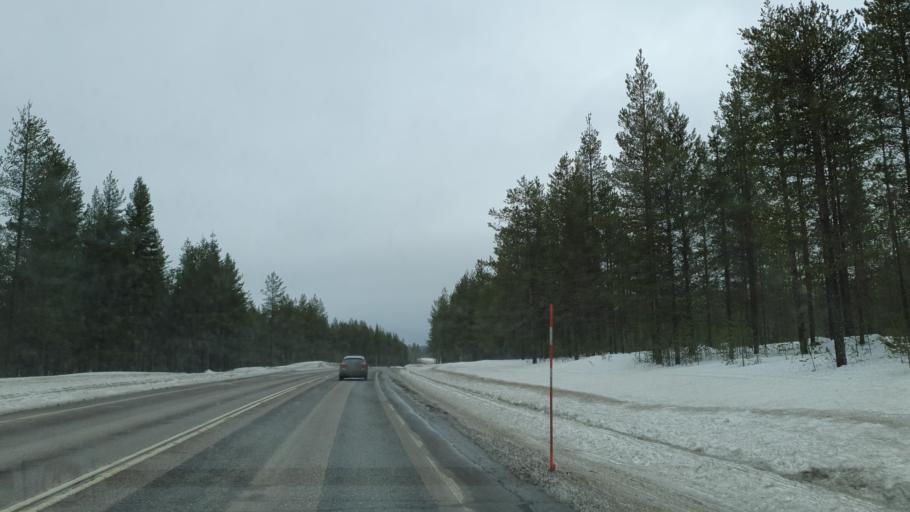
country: FI
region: Lapland
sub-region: Torniolaakso
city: Pello
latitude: 66.9230
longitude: 24.0879
